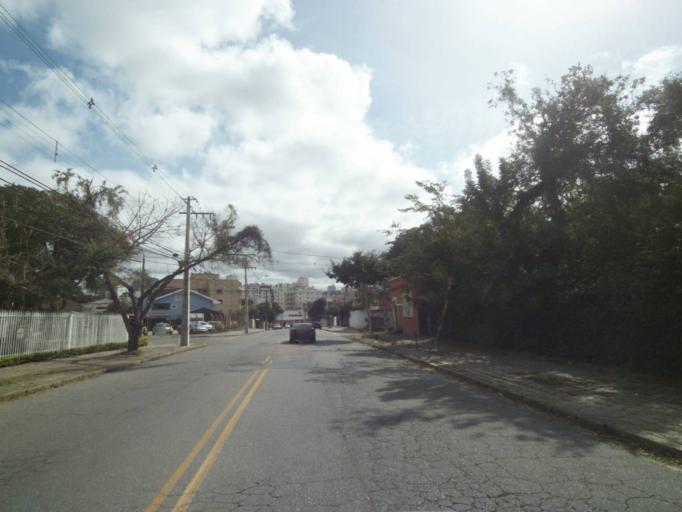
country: BR
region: Parana
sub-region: Curitiba
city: Curitiba
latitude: -25.4646
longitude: -49.2818
